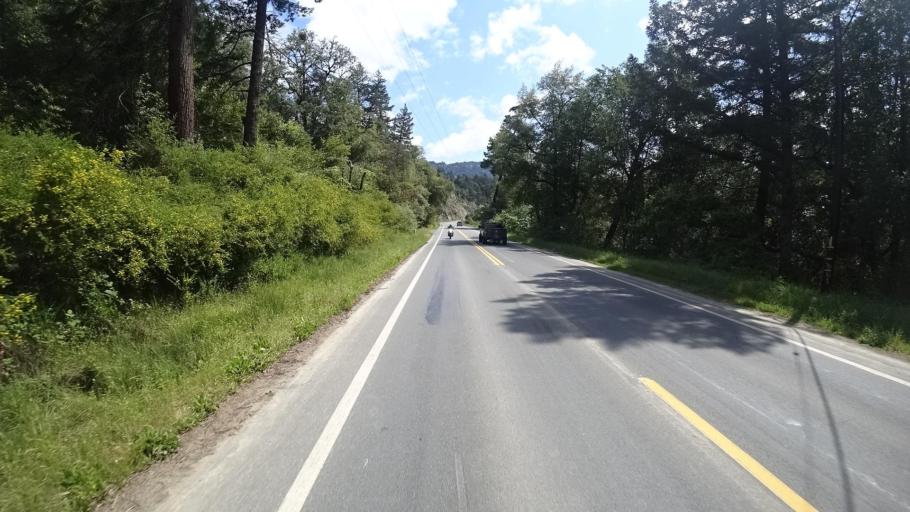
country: US
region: California
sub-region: Humboldt County
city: Redway
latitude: 40.1165
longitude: -123.8035
